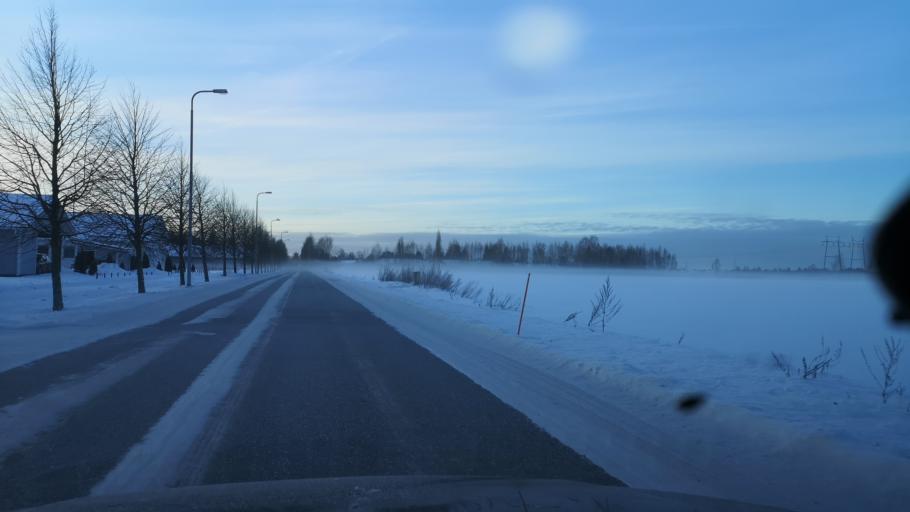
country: FI
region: Satakunta
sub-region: Pori
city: Pori
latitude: 61.5027
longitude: 21.8324
